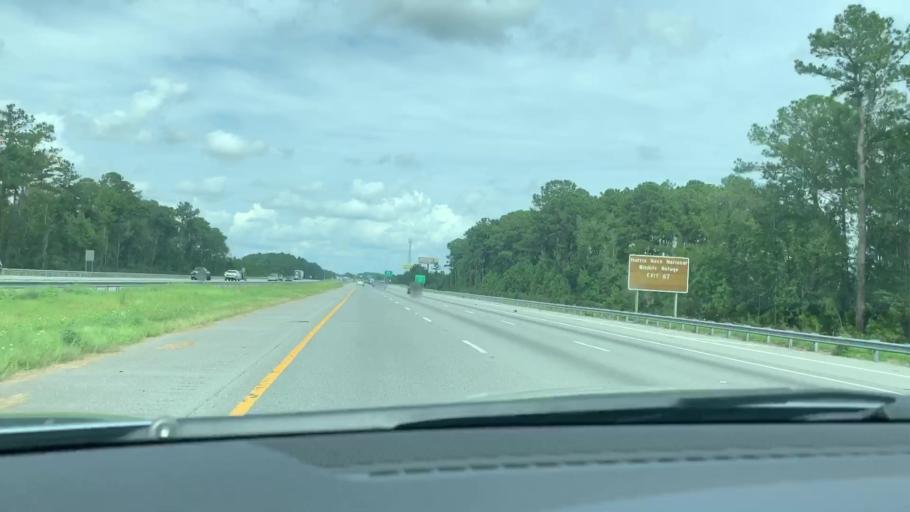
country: US
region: Georgia
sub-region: Liberty County
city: Midway
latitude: 31.6412
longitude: -81.4011
